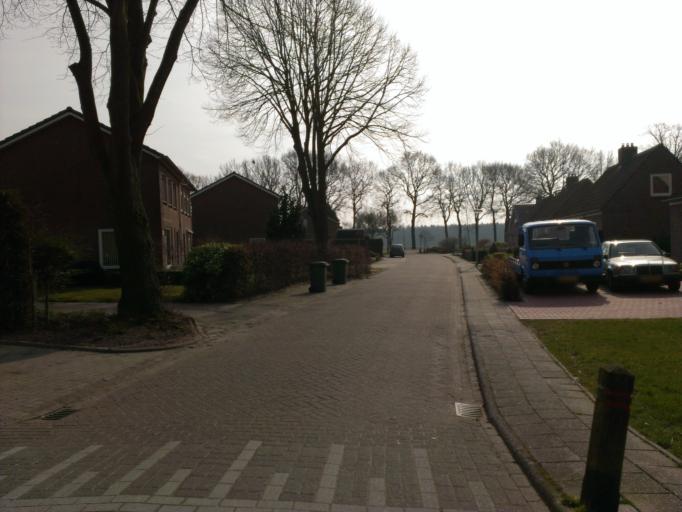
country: NL
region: Drenthe
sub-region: Gemeente Hoogeveen
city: Hoogeveen
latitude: 52.7477
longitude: 6.4989
